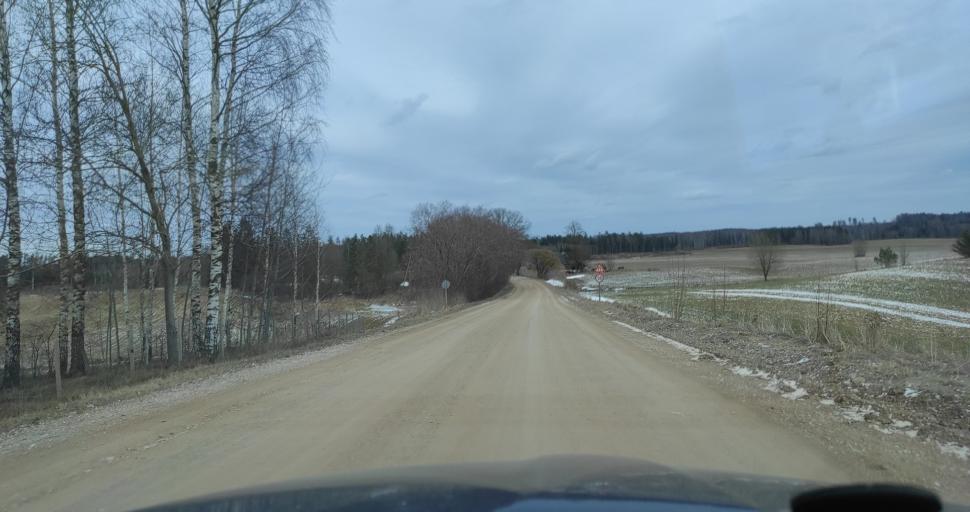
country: LV
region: Tukuma Rajons
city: Tukums
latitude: 57.0267
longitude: 23.0277
